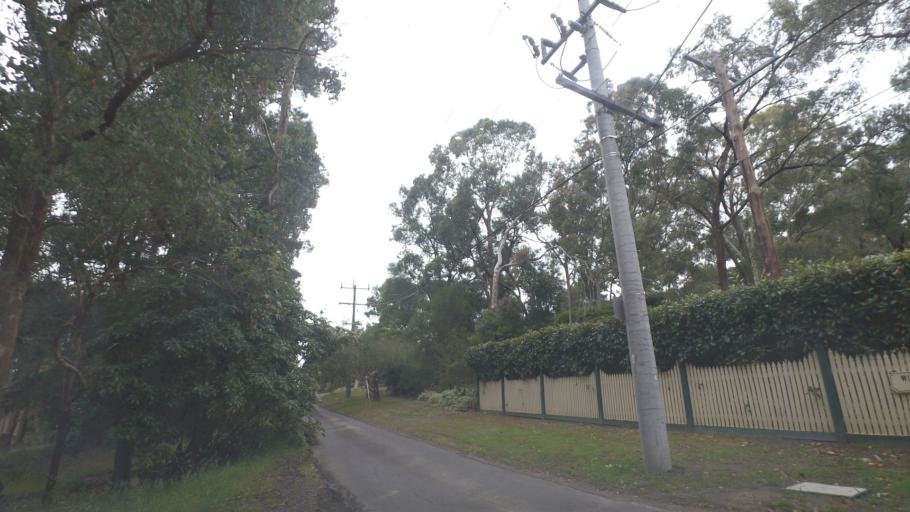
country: AU
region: Victoria
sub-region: Manningham
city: Park Orchards
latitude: -37.7759
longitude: 145.2096
